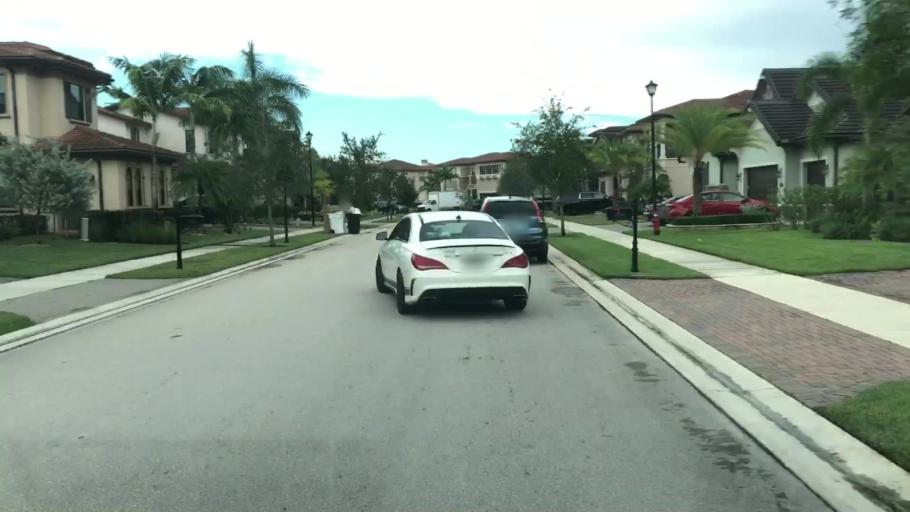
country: US
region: Florida
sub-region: Broward County
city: Parkland
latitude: 26.3426
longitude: -80.2759
